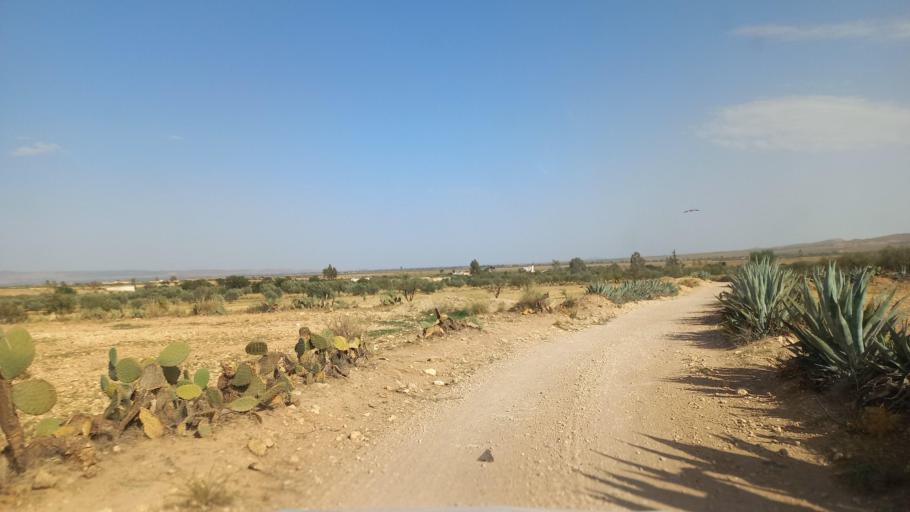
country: TN
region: Al Qasrayn
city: Kasserine
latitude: 35.2509
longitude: 8.9312
